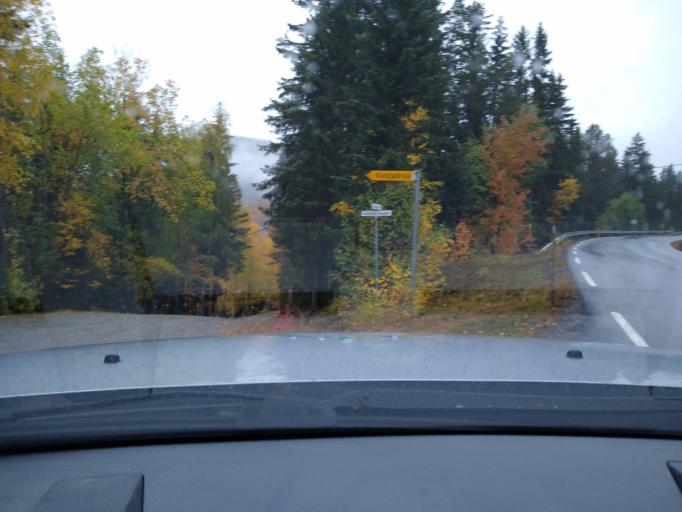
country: NO
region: Oppland
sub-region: Ringebu
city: Ringebu
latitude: 61.5503
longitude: 10.1574
